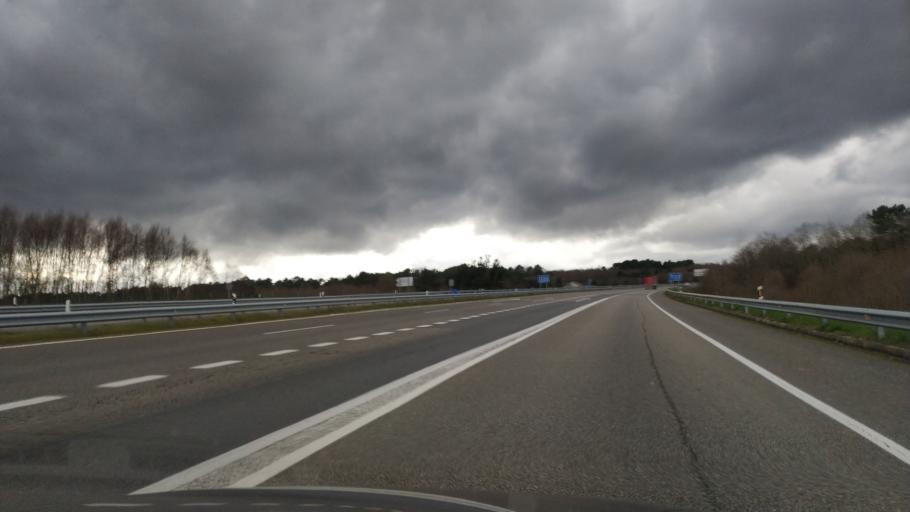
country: ES
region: Galicia
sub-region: Provincia de Ourense
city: Allariz
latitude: 42.2077
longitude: -7.8202
